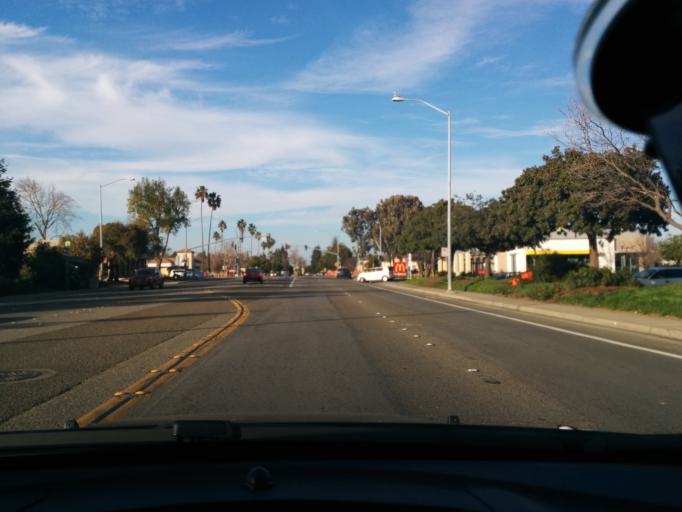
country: US
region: California
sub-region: Santa Clara County
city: Cupertino
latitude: 37.3364
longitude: -122.0414
